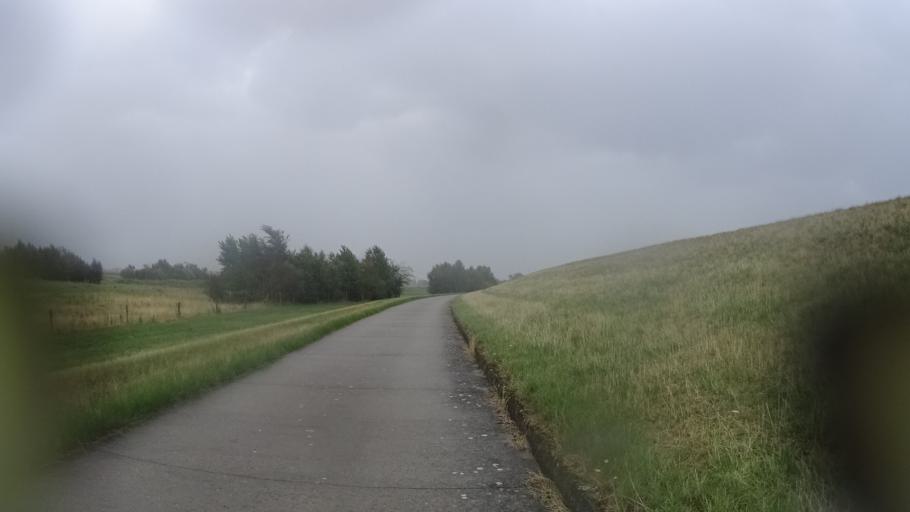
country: DE
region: Lower Saxony
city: Hitzacker
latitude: 53.1784
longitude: 11.0240
